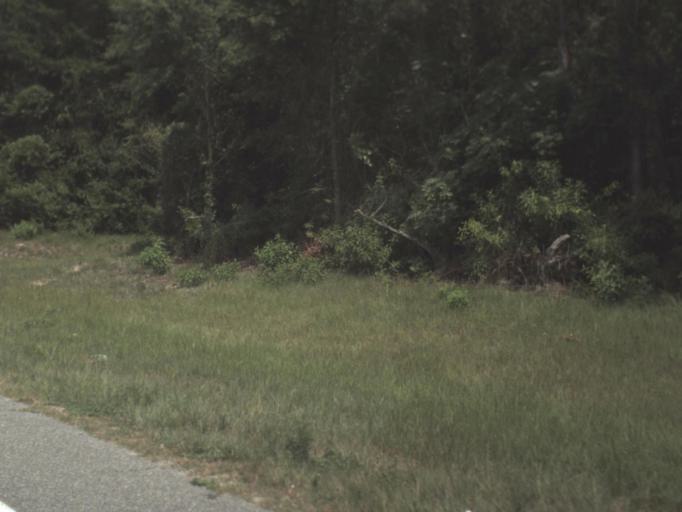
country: US
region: Florida
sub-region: Hamilton County
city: Jasper
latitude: 30.4902
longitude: -83.1169
